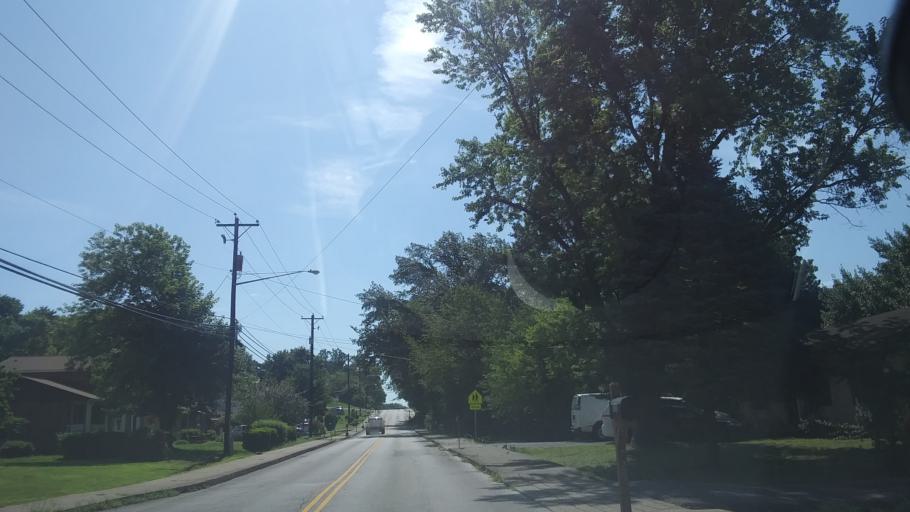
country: US
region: Tennessee
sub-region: Rutherford County
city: La Vergne
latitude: 36.0678
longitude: -86.6672
